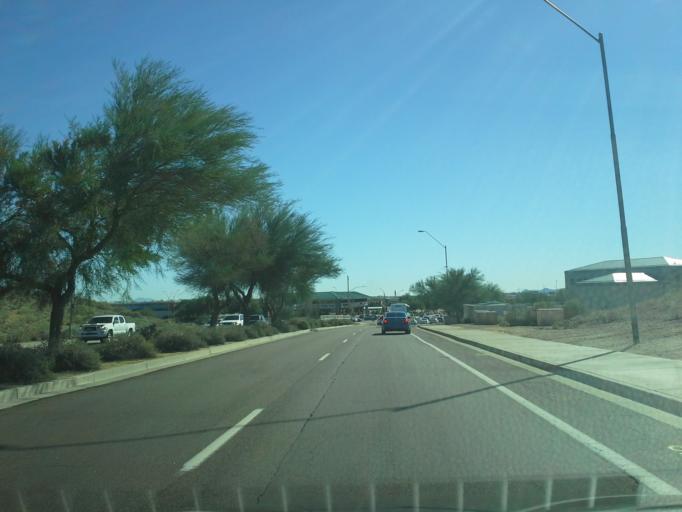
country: US
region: Arizona
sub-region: Maricopa County
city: Paradise Valley
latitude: 33.6364
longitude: -111.9076
